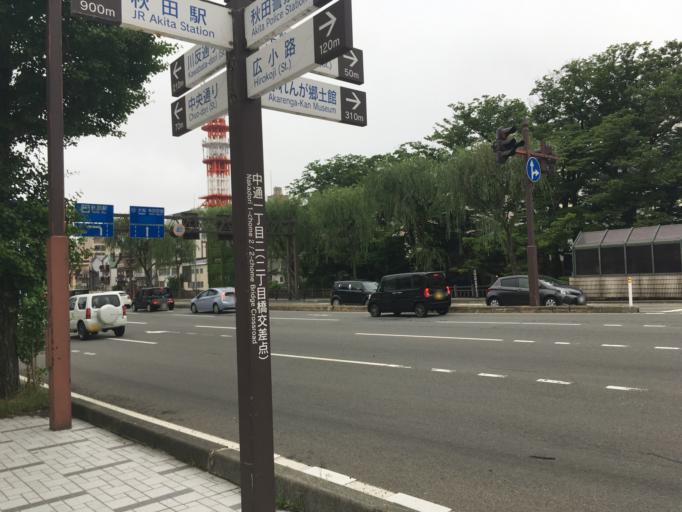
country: JP
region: Akita
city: Akita
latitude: 39.7173
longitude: 140.1185
